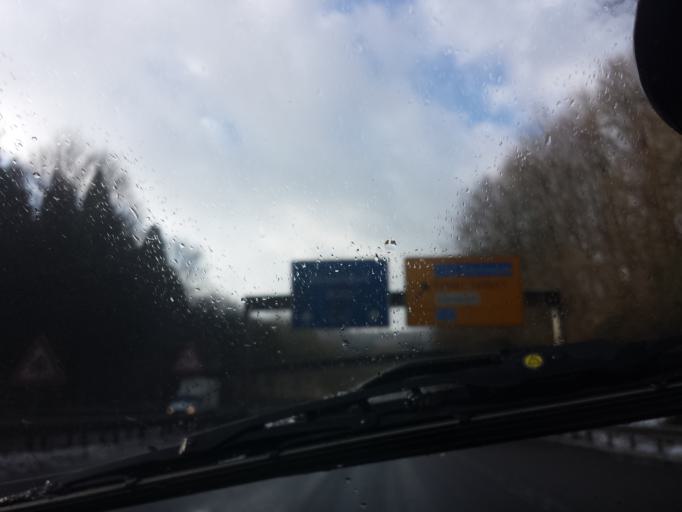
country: DE
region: North Rhine-Westphalia
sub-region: Regierungsbezirk Dusseldorf
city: Solingen
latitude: 51.2320
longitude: 7.1062
